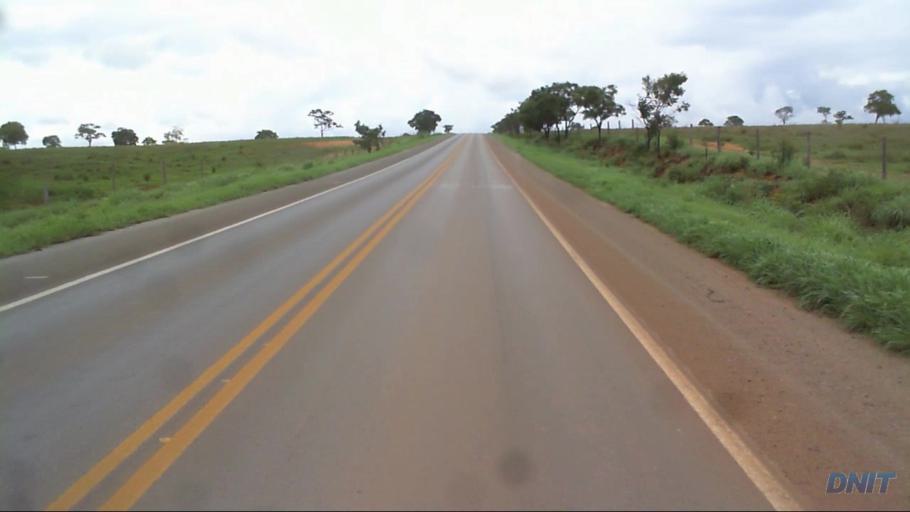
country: BR
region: Goias
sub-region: Padre Bernardo
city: Padre Bernardo
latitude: -15.1579
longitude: -48.3185
